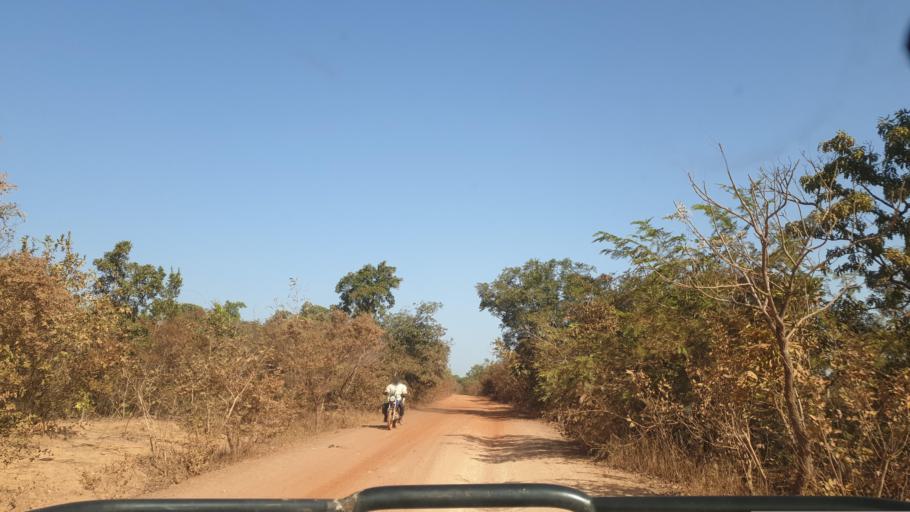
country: ML
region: Sikasso
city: Bougouni
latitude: 11.7800
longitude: -6.9080
